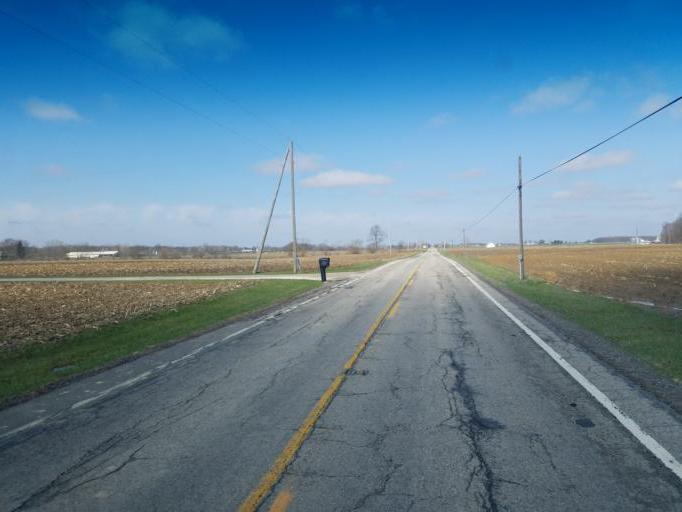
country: US
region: Ohio
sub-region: Crawford County
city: Bucyrus
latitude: 40.8422
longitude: -82.8742
